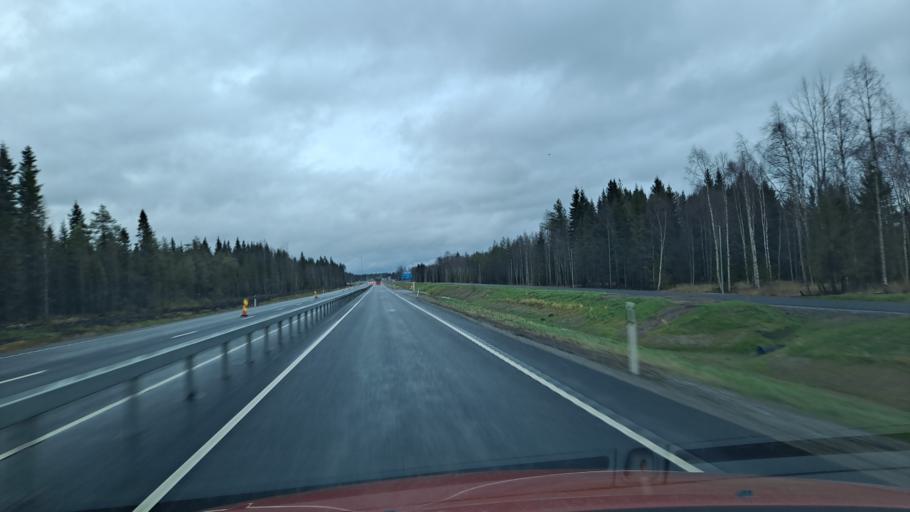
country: FI
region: Lapland
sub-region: Kemi-Tornio
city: Simo
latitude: 65.6730
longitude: 24.9066
